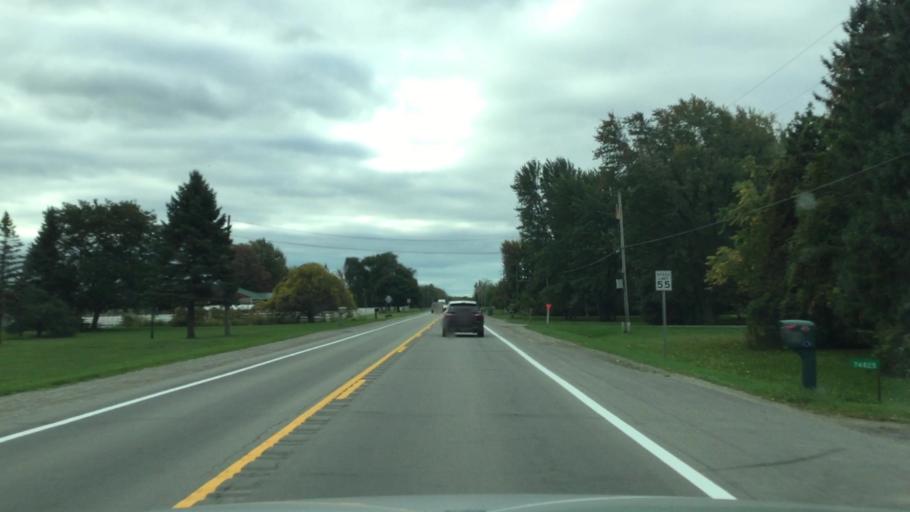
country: US
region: Michigan
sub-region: Macomb County
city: Richmond
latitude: 42.8521
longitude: -82.7633
